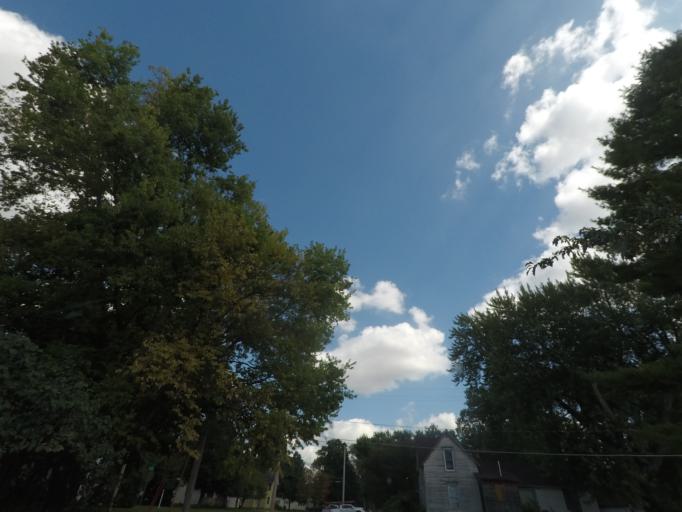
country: US
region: Iowa
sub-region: Story County
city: Nevada
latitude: 42.0216
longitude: -93.4594
